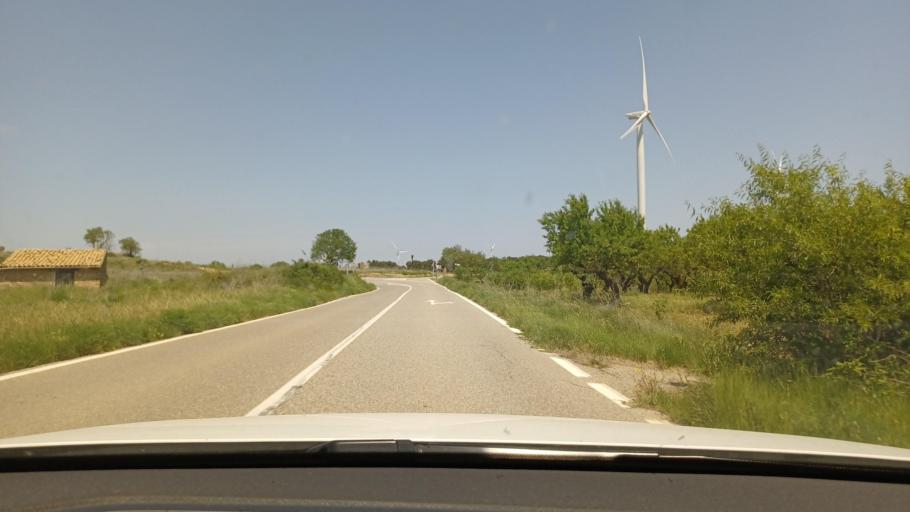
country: ES
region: Catalonia
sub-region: Provincia de Tarragona
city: Vilalba dels Arcs
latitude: 41.1079
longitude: 0.4201
